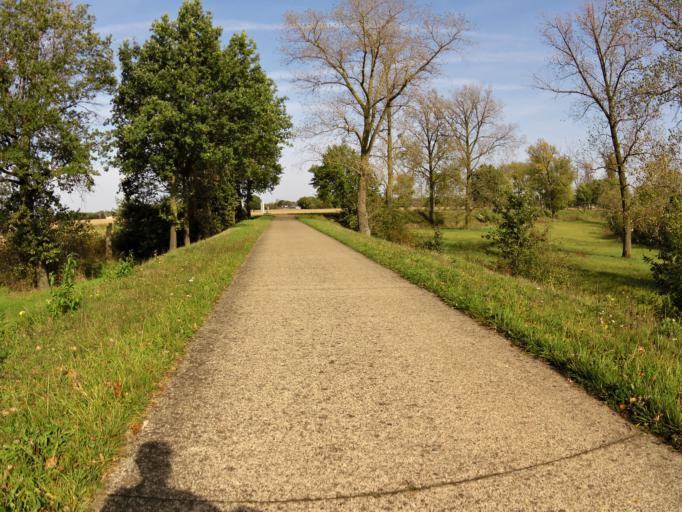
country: BE
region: Flanders
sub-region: Provincie Limburg
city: Maasmechelen
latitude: 50.9832
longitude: 5.7269
